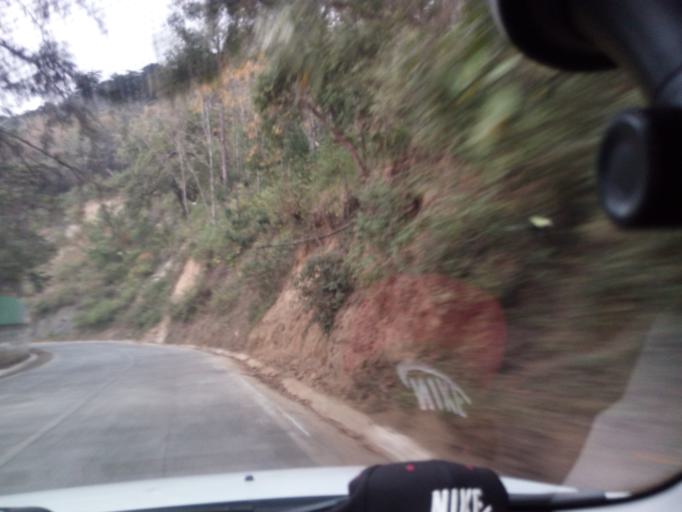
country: GT
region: Sacatepequez
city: Antigua Guatemala
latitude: 14.5711
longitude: -90.7188
